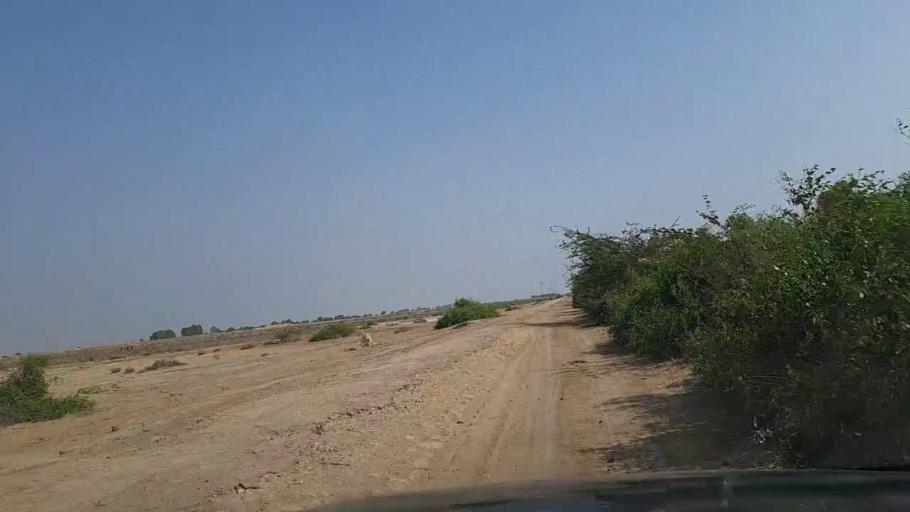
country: PK
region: Sindh
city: Gharo
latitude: 24.7413
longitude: 67.6450
